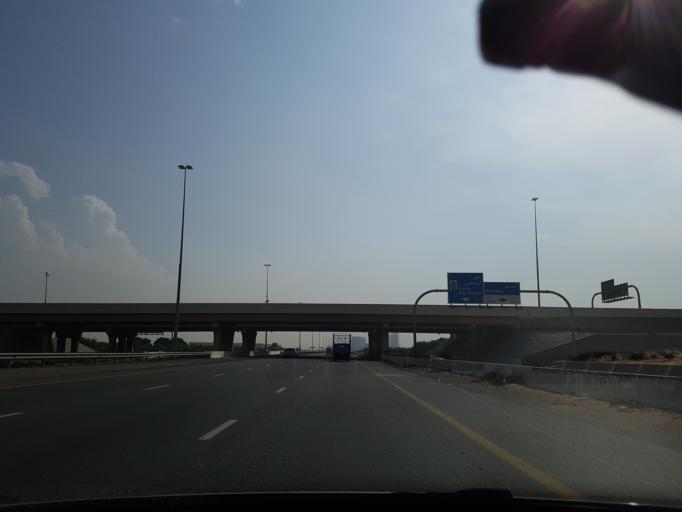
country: AE
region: Umm al Qaywayn
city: Umm al Qaywayn
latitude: 25.4270
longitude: 55.5930
